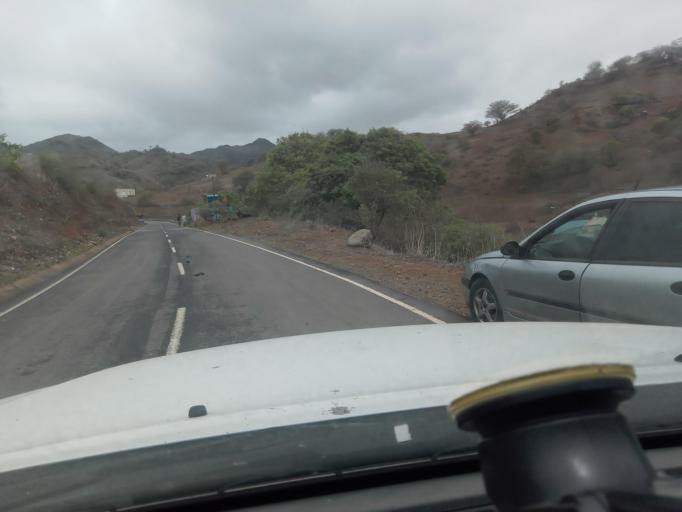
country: CV
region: Sao Miguel
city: Calheta
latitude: 15.1459
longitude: -23.6201
